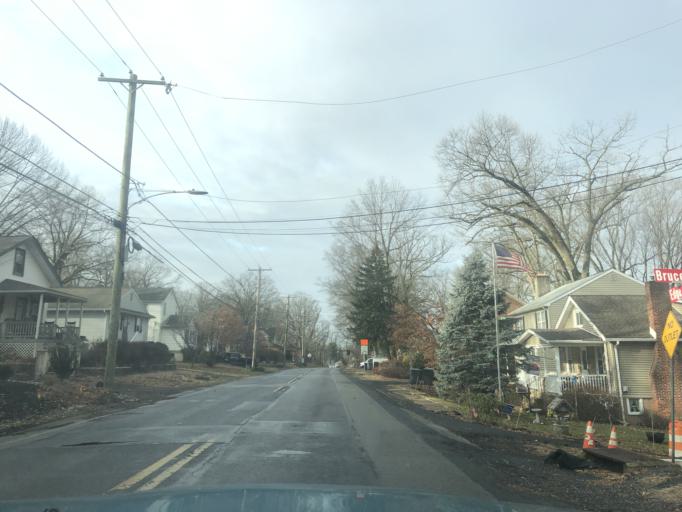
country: US
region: Pennsylvania
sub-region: Montgomery County
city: Glenside
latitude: 40.1159
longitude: -75.1466
